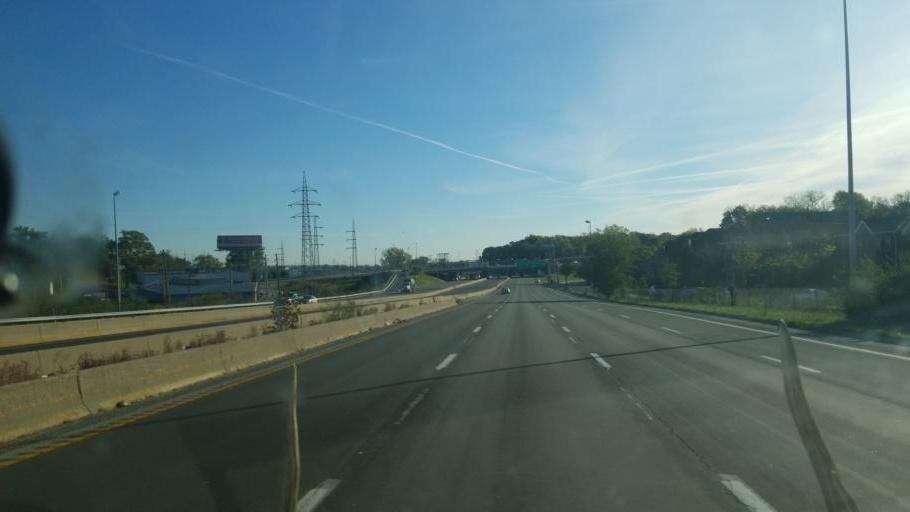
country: US
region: Missouri
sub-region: Saint Louis County
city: Pine Lawn
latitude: 38.6828
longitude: -90.2329
